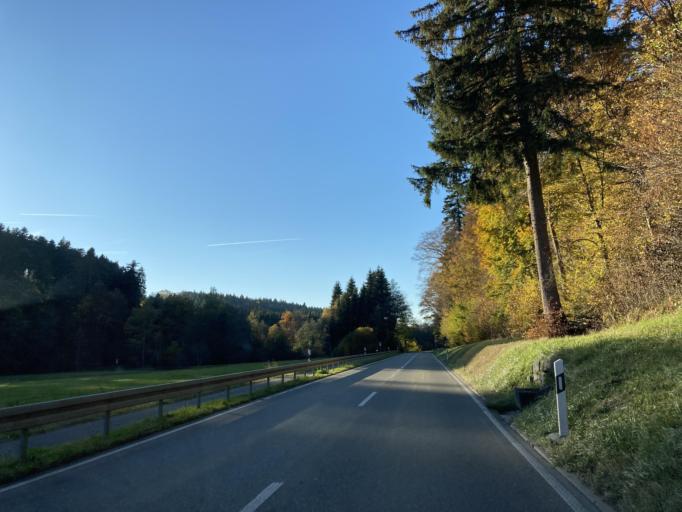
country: DE
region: Baden-Wuerttemberg
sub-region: Tuebingen Region
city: Bodelshausen
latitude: 48.4251
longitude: 8.9790
